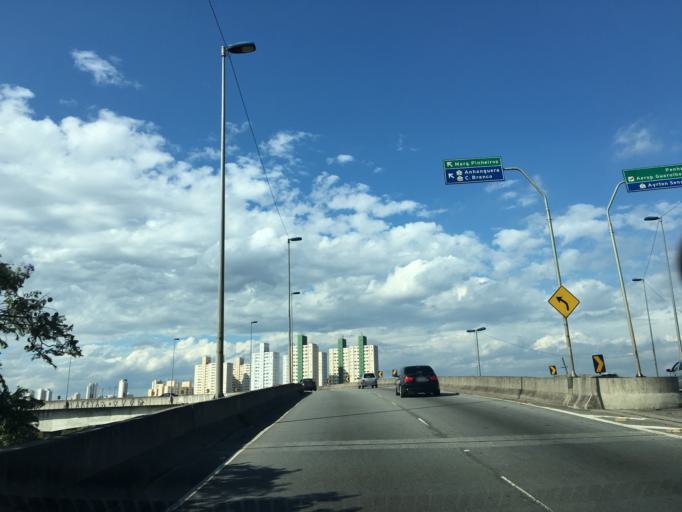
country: BR
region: Sao Paulo
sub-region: Sao Paulo
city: Sao Paulo
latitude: -23.5288
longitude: -46.5833
